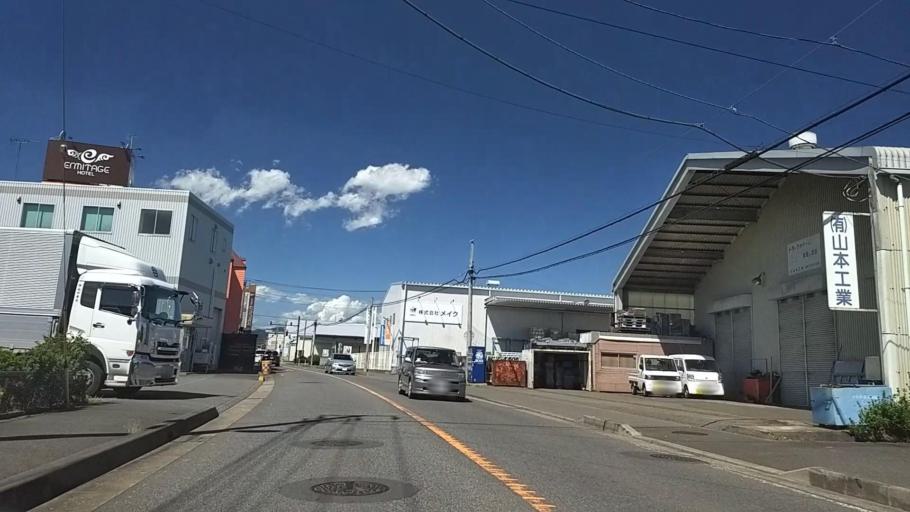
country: JP
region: Tokyo
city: Hachioji
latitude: 35.5638
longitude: 139.3257
